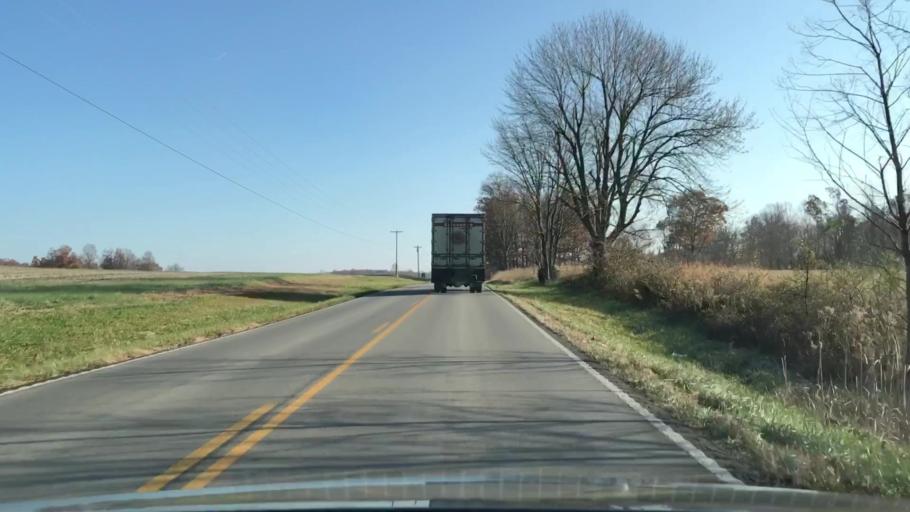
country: US
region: Kentucky
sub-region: Edmonson County
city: Brownsville
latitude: 37.3292
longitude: -86.2585
